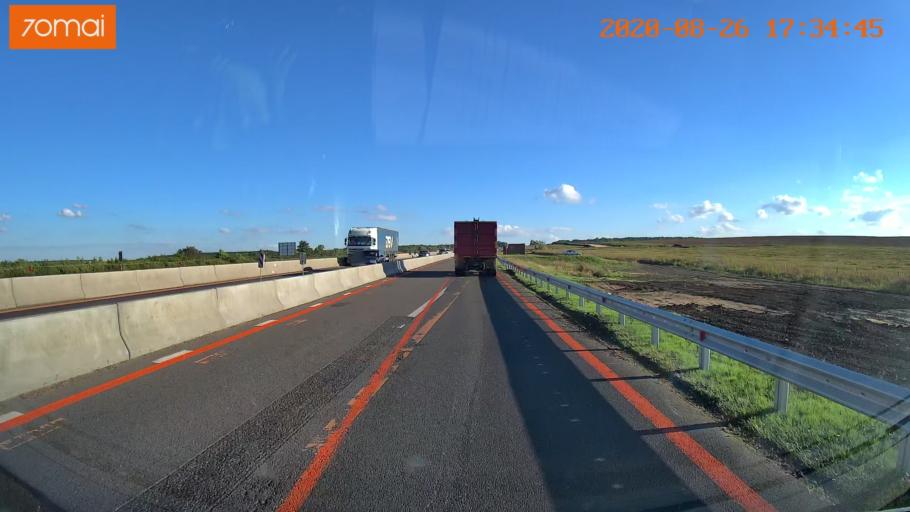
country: RU
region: Tula
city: Kazachka
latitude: 53.3960
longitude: 38.1846
